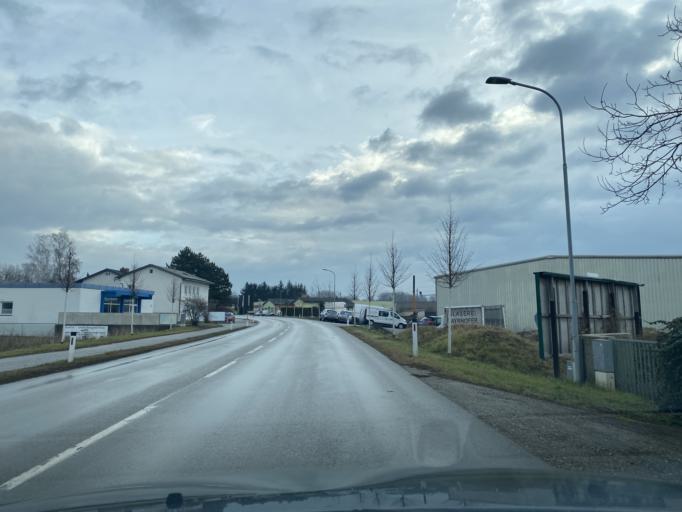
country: AT
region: Lower Austria
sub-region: Politischer Bezirk Sankt Polten
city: Prinzersdorf
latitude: 48.1998
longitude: 15.5051
